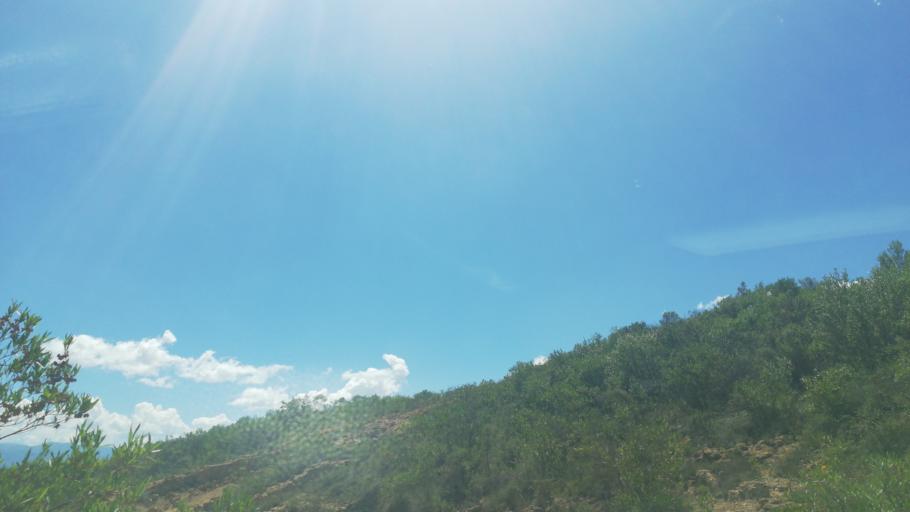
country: BO
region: Cochabamba
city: Totora
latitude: -17.7358
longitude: -65.2235
